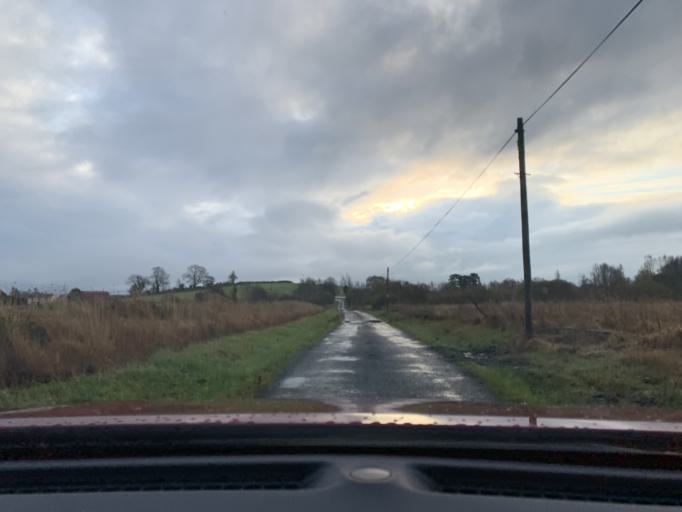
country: IE
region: Connaught
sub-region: Sligo
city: Ballymote
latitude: 54.0299
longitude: -8.5261
